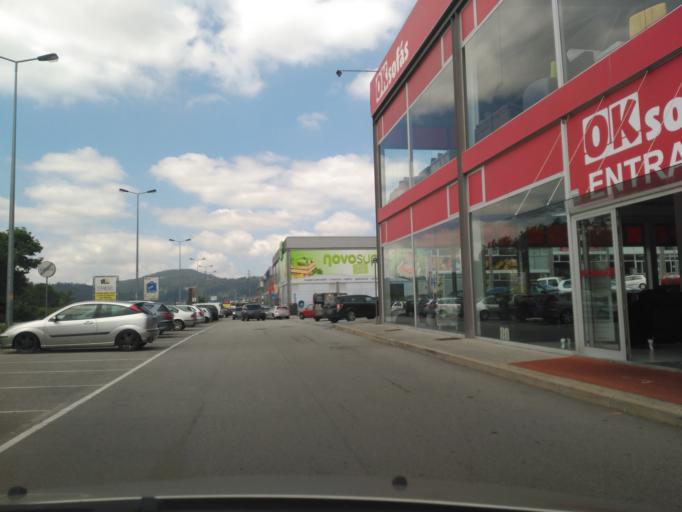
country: PT
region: Braga
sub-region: Braga
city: Braga
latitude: 41.5333
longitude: -8.4656
